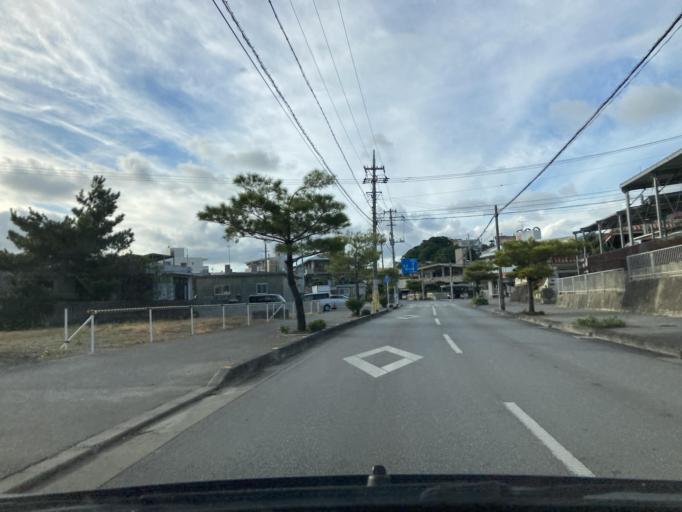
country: JP
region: Okinawa
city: Itoman
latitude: 26.1378
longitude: 127.7420
